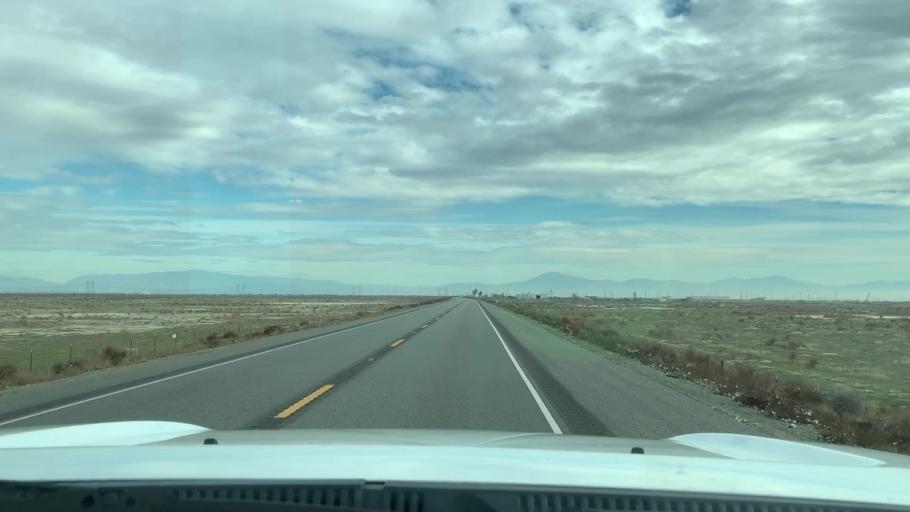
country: US
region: California
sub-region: Kern County
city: Rosedale
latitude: 35.2674
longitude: -119.2736
